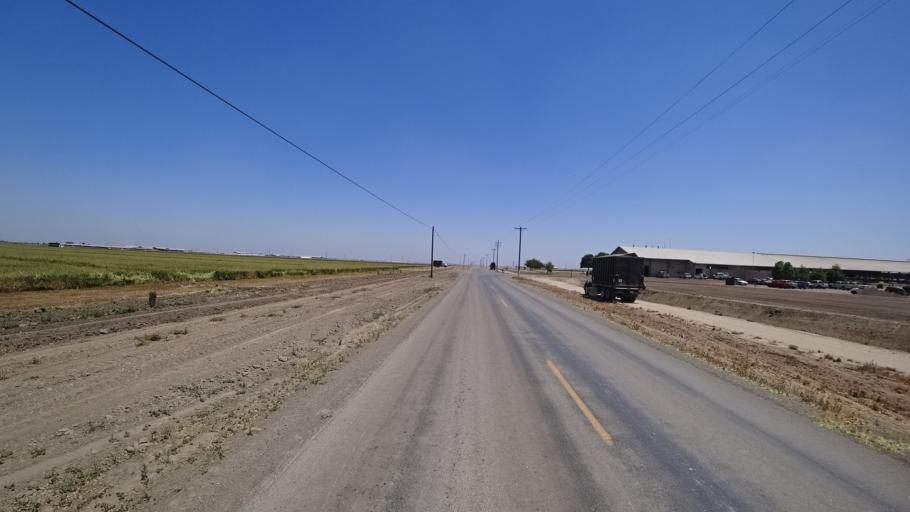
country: US
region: California
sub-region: Kings County
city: Corcoran
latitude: 36.1965
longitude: -119.6069
